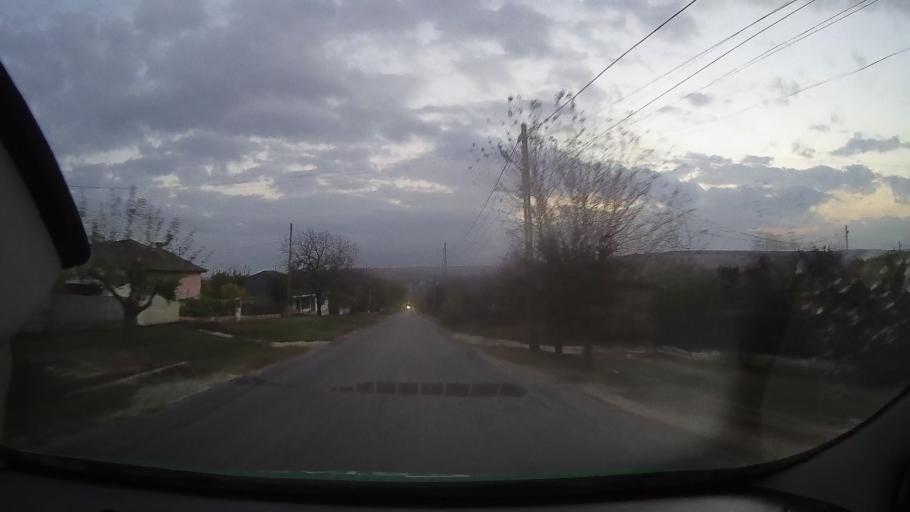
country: RO
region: Constanta
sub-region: Comuna Baneasa
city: Baneasa
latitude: 44.0757
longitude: 27.6963
